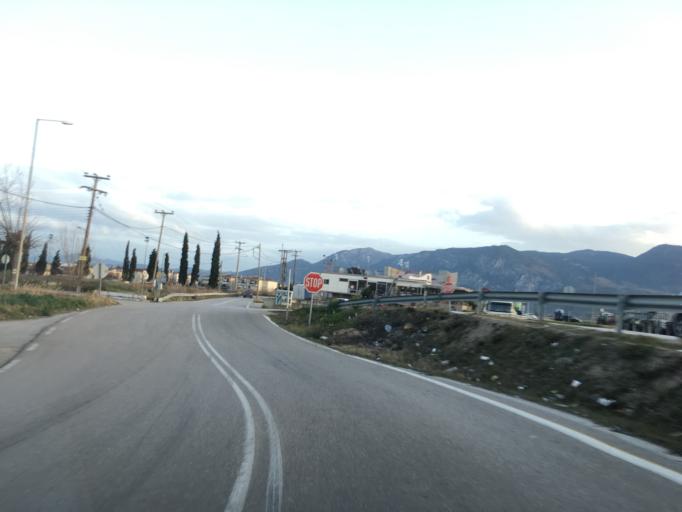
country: GR
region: Central Greece
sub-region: Nomos Fthiotidos
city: Anthili
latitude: 38.8485
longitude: 22.4711
